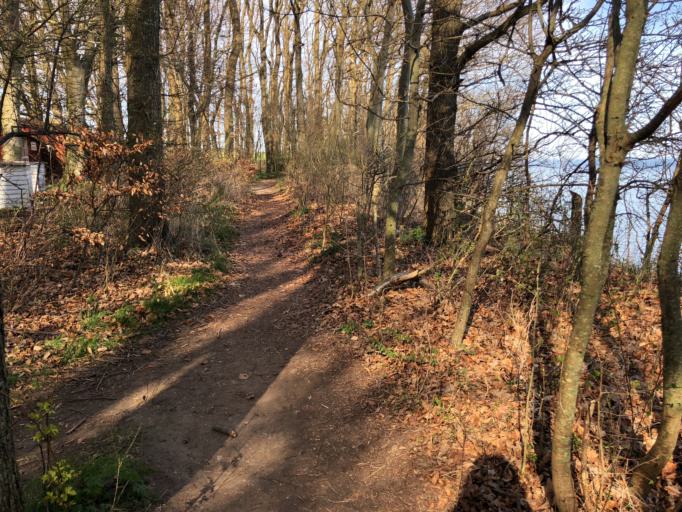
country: DK
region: Zealand
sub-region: Stevns Kommune
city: Store Heddinge
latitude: 55.2816
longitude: 12.4479
